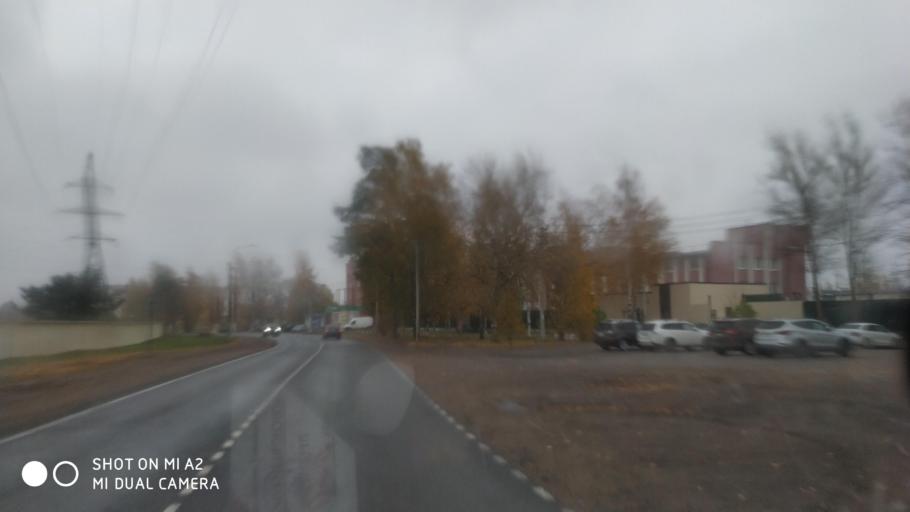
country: RU
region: Leningrad
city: Sosnovyy Bor
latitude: 59.8930
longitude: 29.1083
